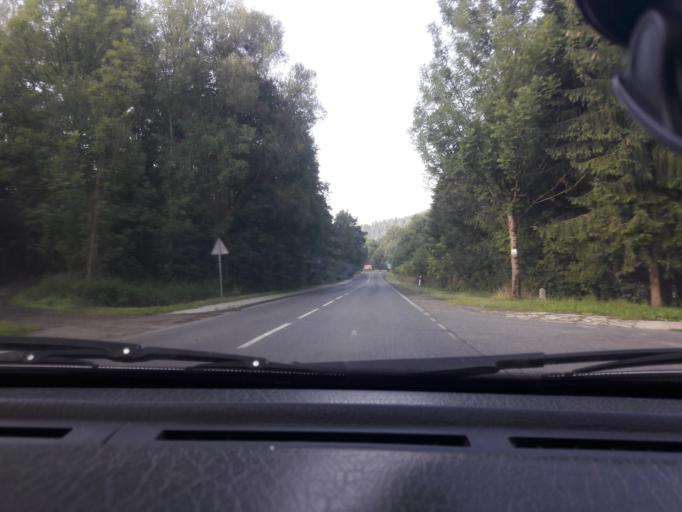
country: PL
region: Lesser Poland Voivodeship
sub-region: Powiat suski
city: Zawoja
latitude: 49.6378
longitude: 19.5309
